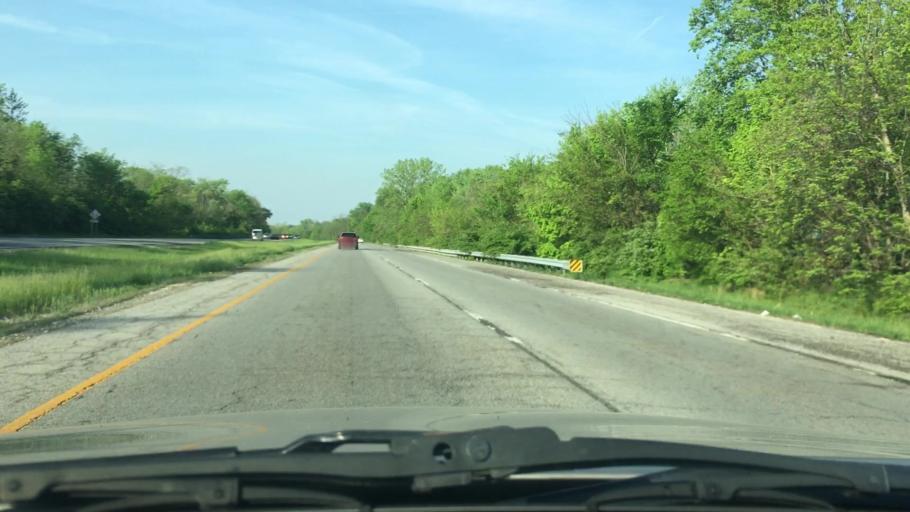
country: US
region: Indiana
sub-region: Marion County
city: Broad Ripple
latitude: 39.8675
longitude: -86.0857
